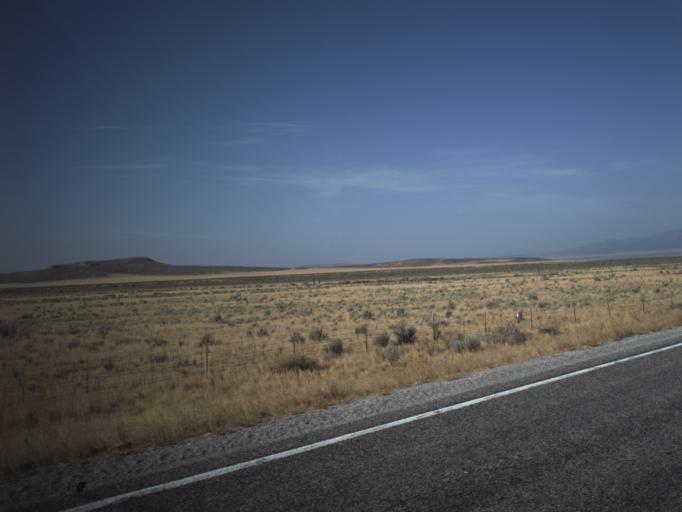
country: US
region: Idaho
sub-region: Oneida County
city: Malad City
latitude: 41.9636
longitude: -112.7625
